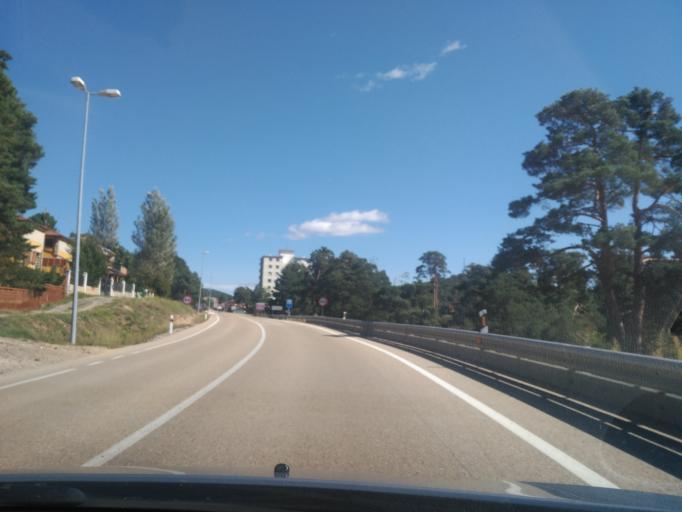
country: ES
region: Castille and Leon
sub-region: Provincia de Soria
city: Navaleno
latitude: 41.8379
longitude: -3.0152
